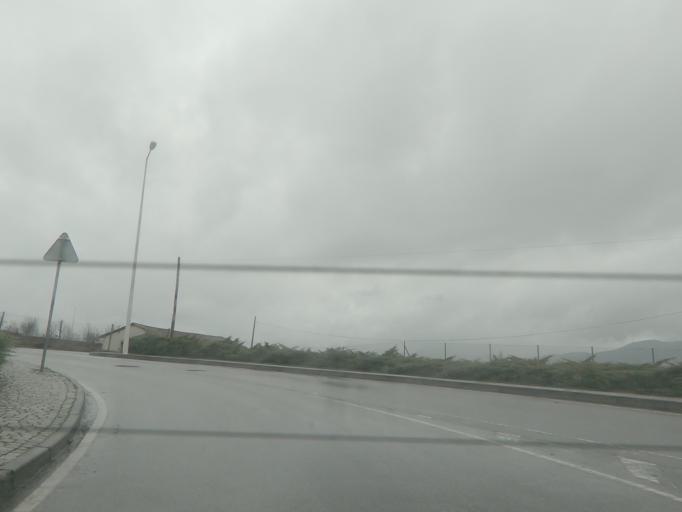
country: PT
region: Vila Real
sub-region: Vila Real
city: Vila Real
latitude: 41.2857
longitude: -7.7346
